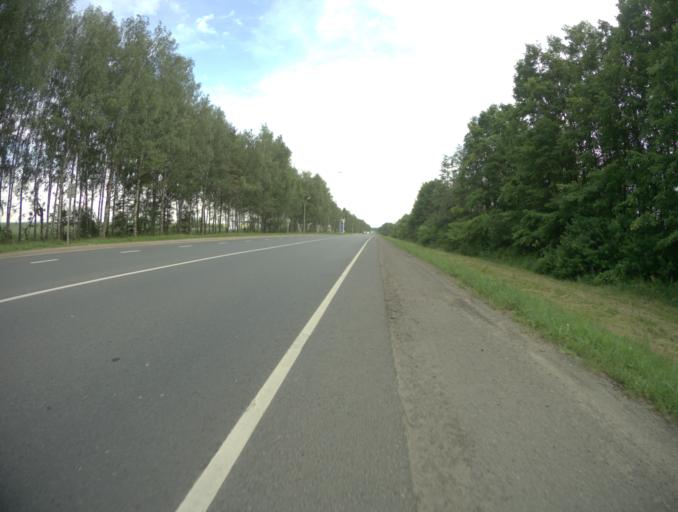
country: RU
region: Vladimir
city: Suzdal'
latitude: 56.3739
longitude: 40.4612
